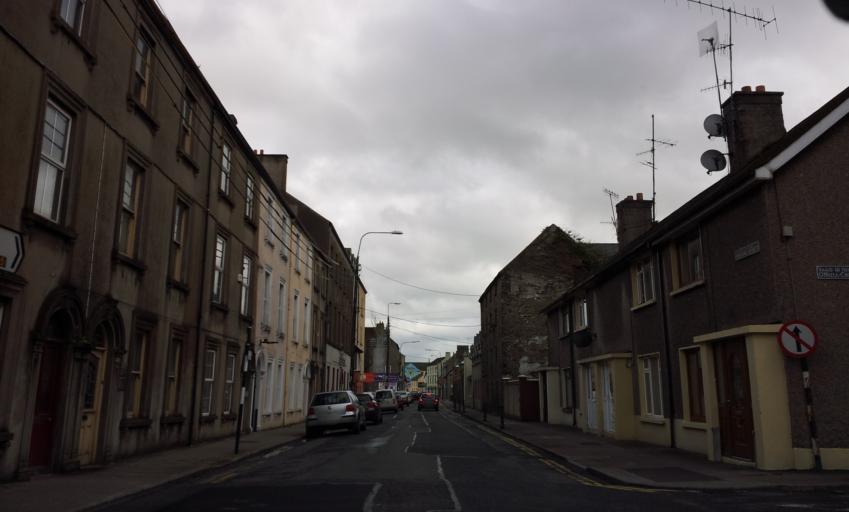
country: IE
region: Munster
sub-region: County Cork
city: Youghal
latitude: 51.9555
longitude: -7.8483
